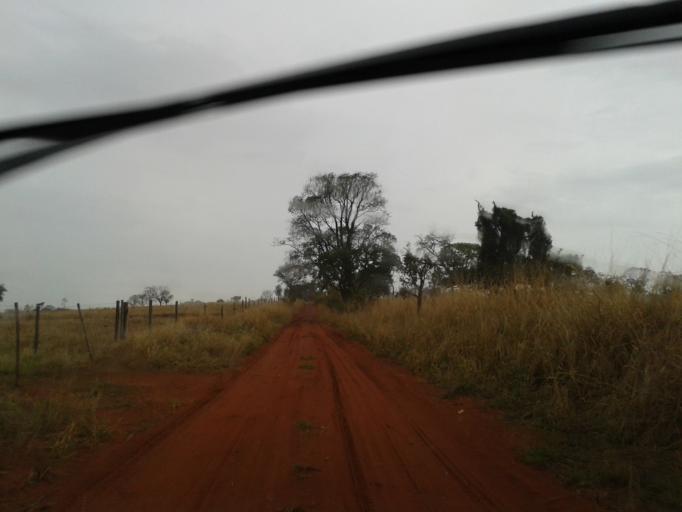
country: BR
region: Minas Gerais
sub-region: Campina Verde
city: Campina Verde
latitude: -19.3537
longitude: -49.5441
